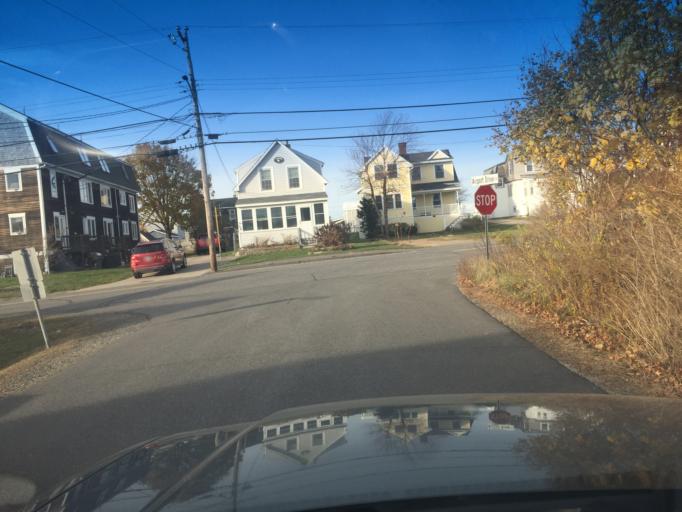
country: US
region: Maine
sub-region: York County
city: York Beach
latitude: 43.1722
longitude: -70.6048
